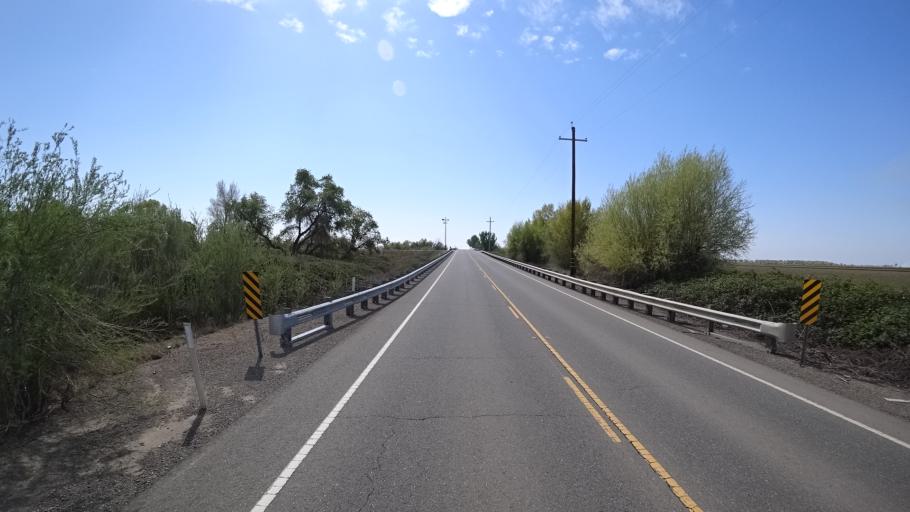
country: US
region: California
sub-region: Butte County
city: Durham
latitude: 39.5360
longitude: -121.8565
